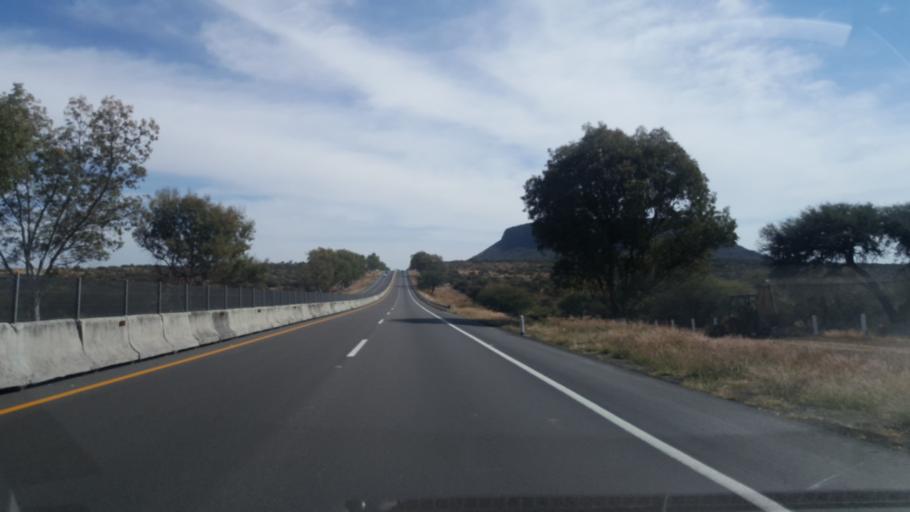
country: MX
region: Jalisco
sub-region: Lagos de Moreno
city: Cristeros [Fraccionamiento]
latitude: 21.3029
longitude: -102.0223
